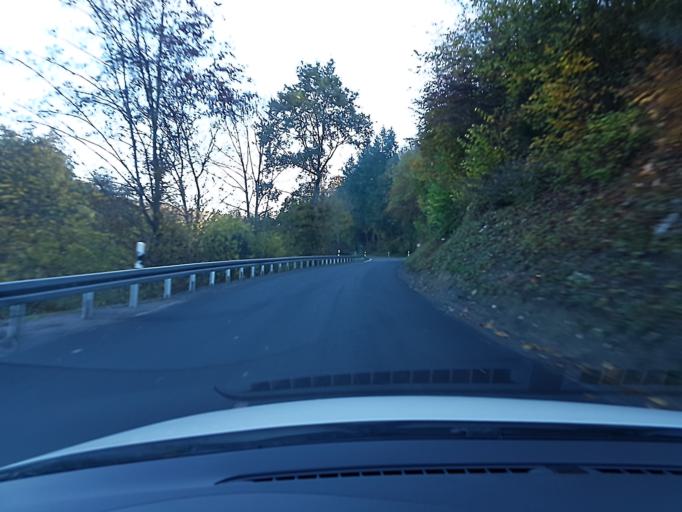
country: DE
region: Baden-Wuerttemberg
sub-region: Regierungsbezirk Stuttgart
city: Neudenau
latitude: 49.2850
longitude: 9.2382
